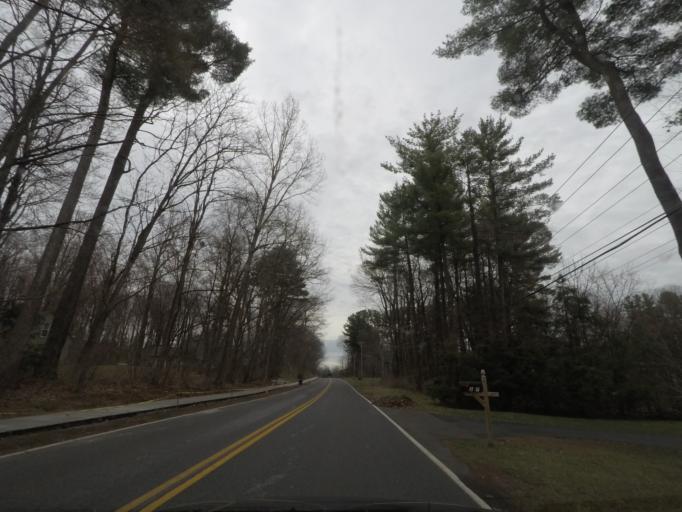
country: US
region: New York
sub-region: Albany County
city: Delmar
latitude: 42.6010
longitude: -73.8258
